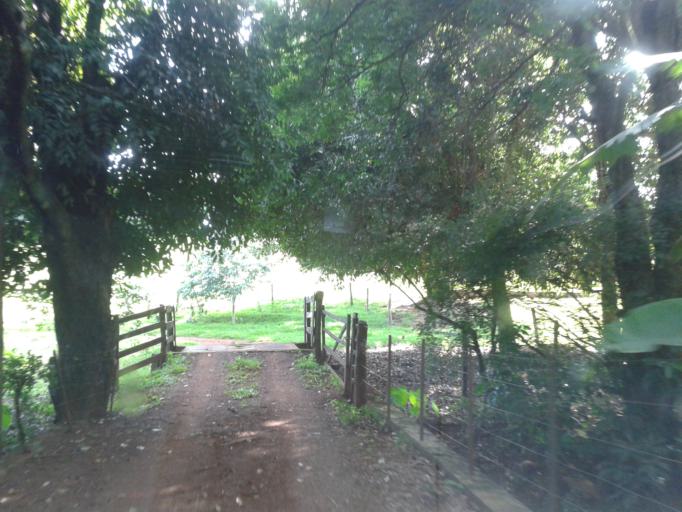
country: BR
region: Minas Gerais
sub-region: Centralina
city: Centralina
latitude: -18.7096
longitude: -49.1881
